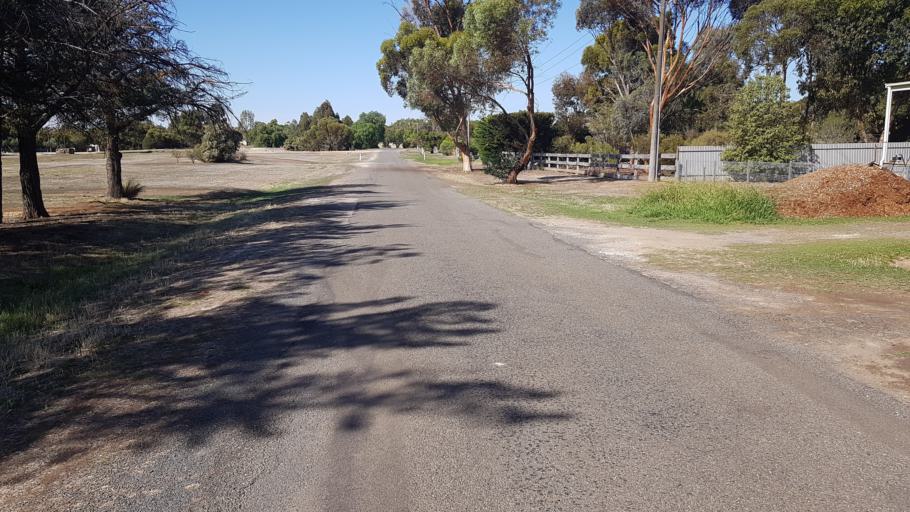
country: AU
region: Victoria
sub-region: Horsham
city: Horsham
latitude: -36.7454
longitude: 141.9401
